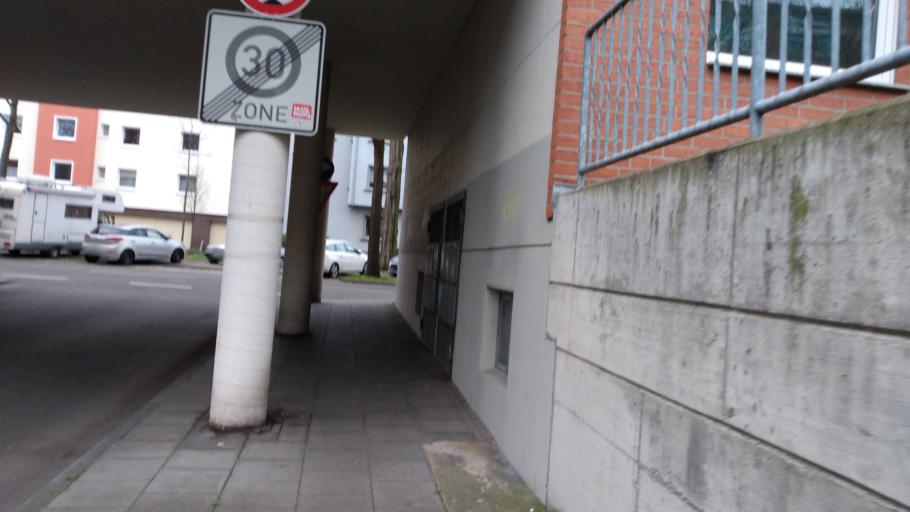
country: DE
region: North Rhine-Westphalia
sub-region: Regierungsbezirk Koln
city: Neustadt/Sued
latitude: 50.9022
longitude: 6.9458
